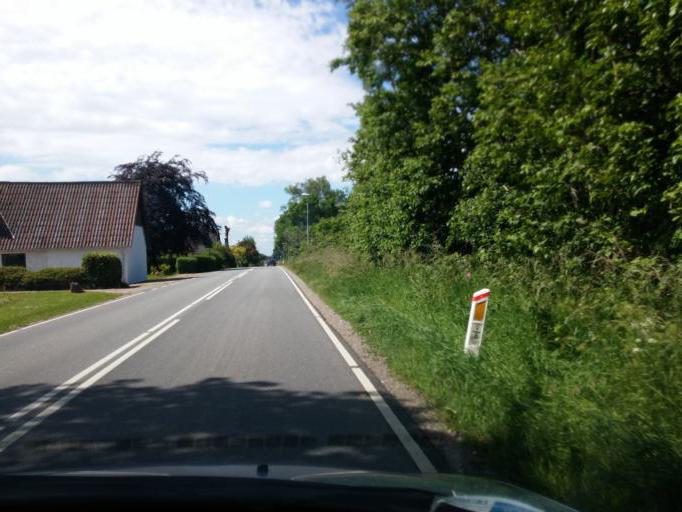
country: DK
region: South Denmark
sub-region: Kerteminde Kommune
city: Langeskov
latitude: 55.3898
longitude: 10.5342
